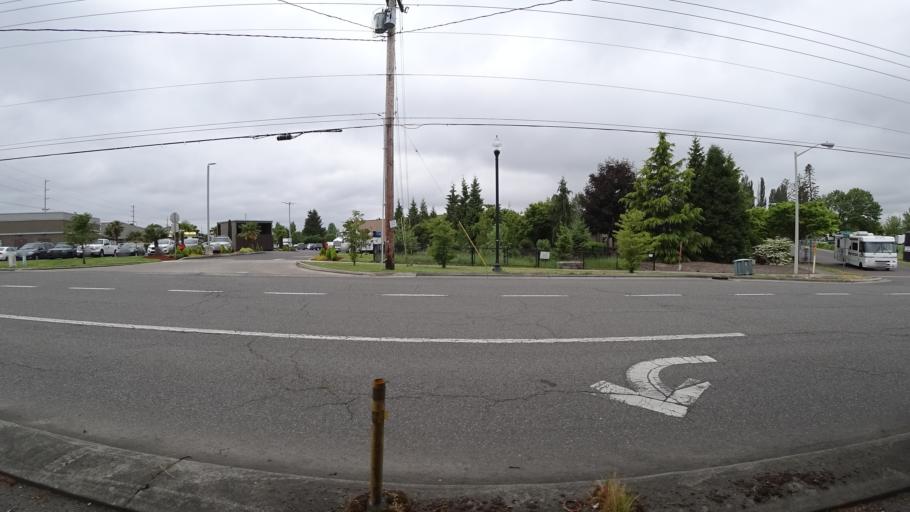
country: US
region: Oregon
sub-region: Washington County
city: Rockcreek
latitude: 45.5669
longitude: -122.8948
